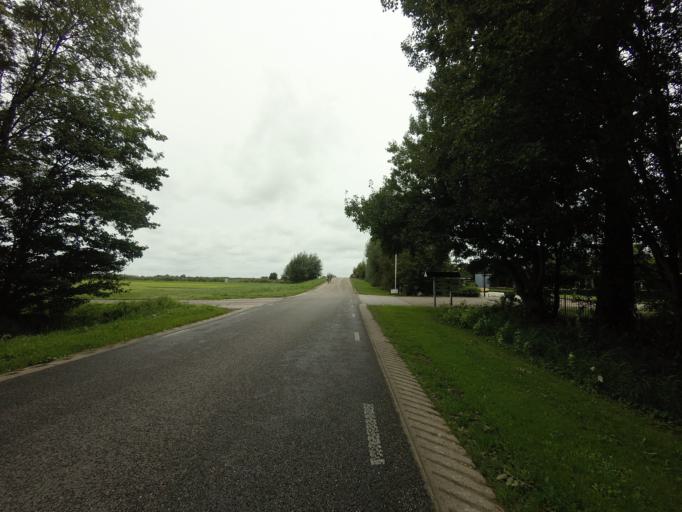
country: NL
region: Overijssel
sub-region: Gemeente Steenwijkerland
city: Oldemarkt
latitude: 52.8127
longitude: 5.9091
